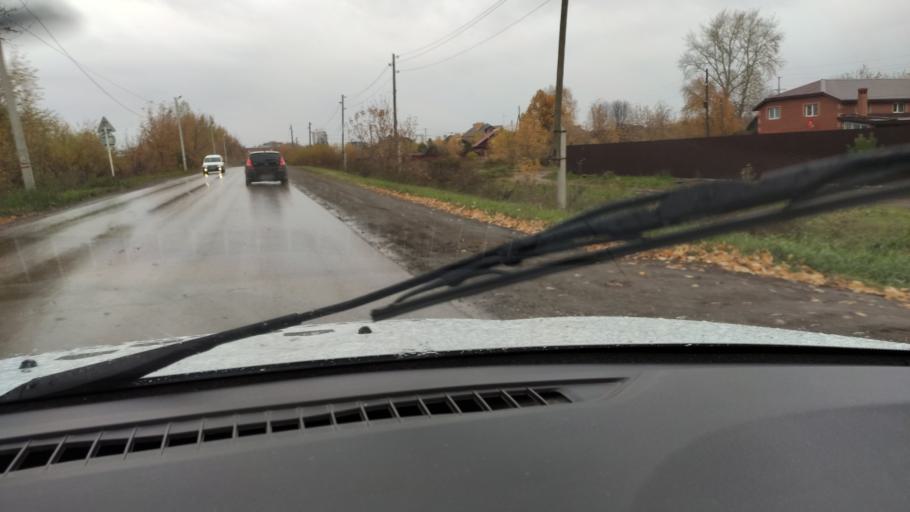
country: RU
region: Perm
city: Kondratovo
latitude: 57.9673
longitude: 56.1179
